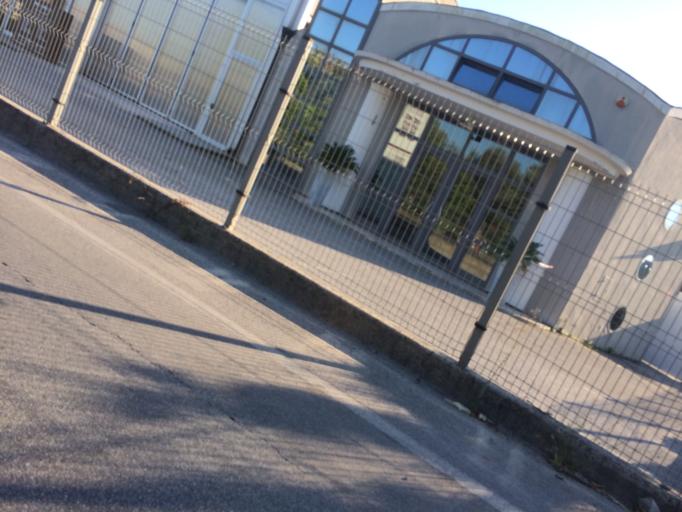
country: IT
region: Tuscany
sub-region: Provincia di Lucca
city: Viareggio
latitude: 43.8619
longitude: 10.2700
